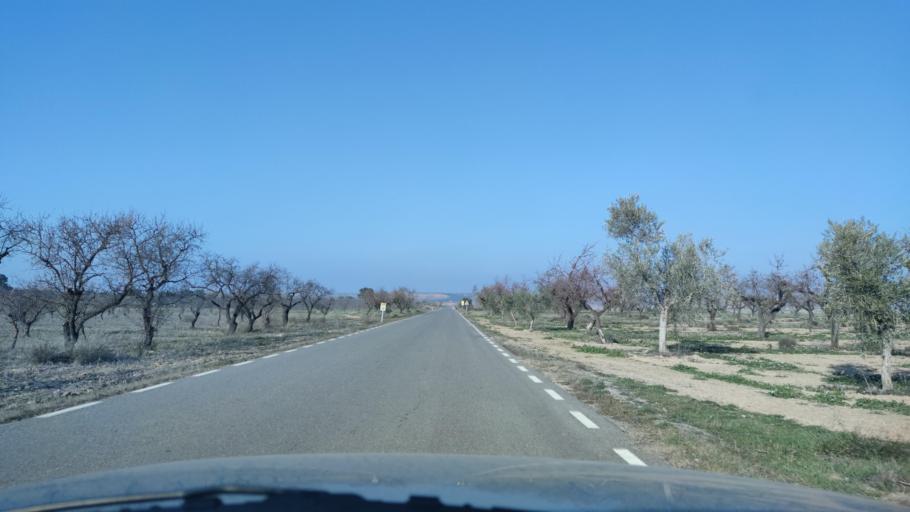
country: ES
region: Catalonia
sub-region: Provincia de Lleida
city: Sunyer
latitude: 41.4938
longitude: 0.5603
